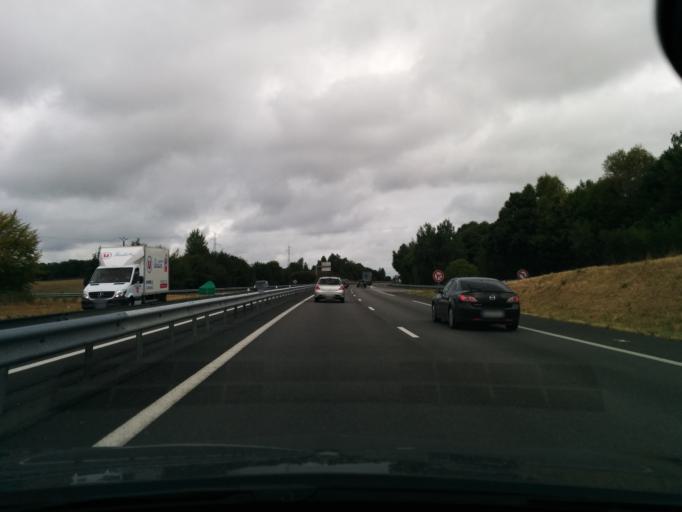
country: FR
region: Limousin
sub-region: Departement de la Haute-Vienne
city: Saint-Germain-les-Belles
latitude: 45.5280
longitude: 1.5132
